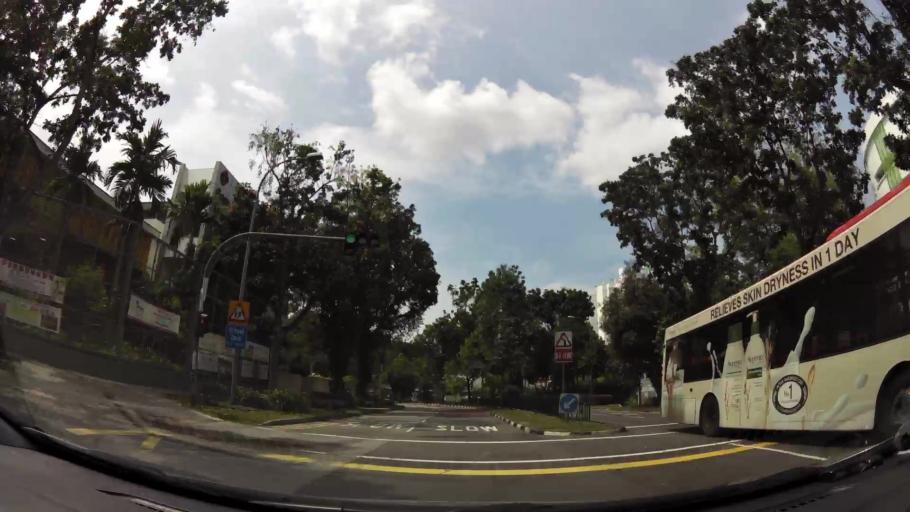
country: MY
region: Johor
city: Johor Bahru
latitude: 1.3489
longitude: 103.7113
